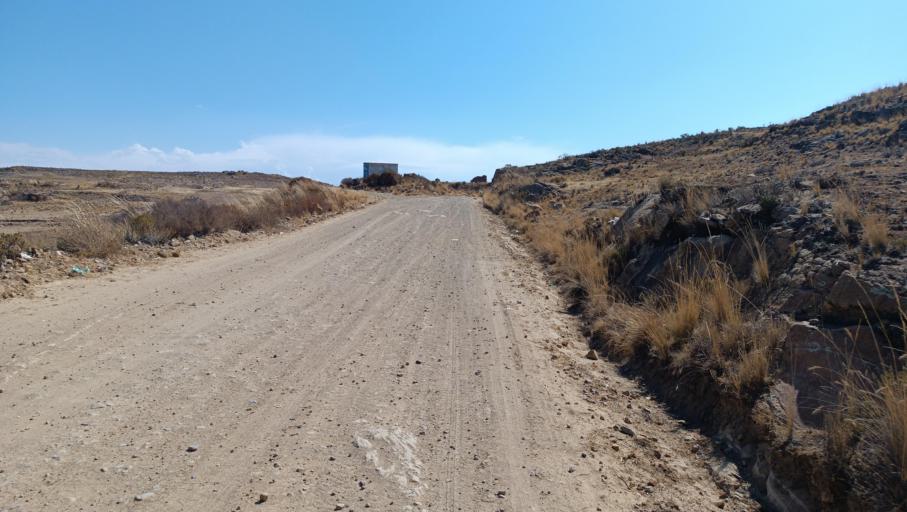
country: BO
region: La Paz
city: Batallas
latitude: -16.3482
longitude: -68.6715
